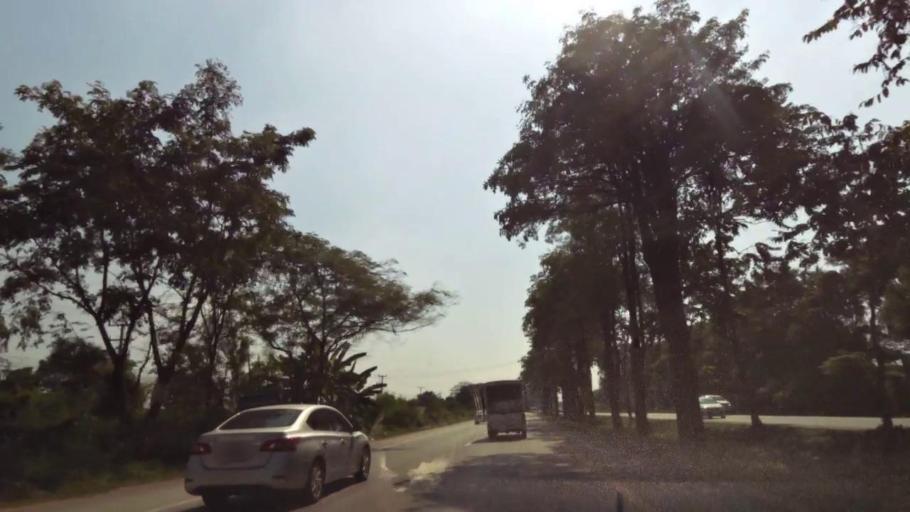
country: TH
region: Phichit
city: Bueng Na Rang
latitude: 16.1170
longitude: 100.1257
